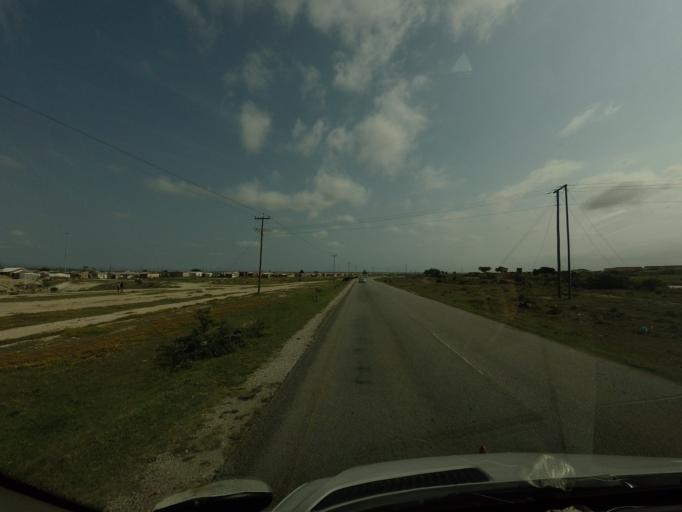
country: ZA
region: Eastern Cape
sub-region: Nelson Mandela Bay Metropolitan Municipality
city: Port Elizabeth
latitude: -33.7785
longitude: 25.5903
